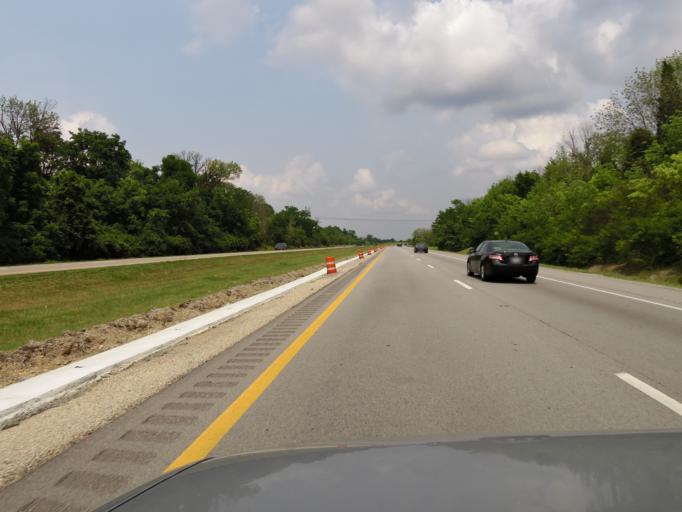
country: US
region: Indiana
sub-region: Switzerland County
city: Vevay
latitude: 38.6703
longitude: -85.0166
